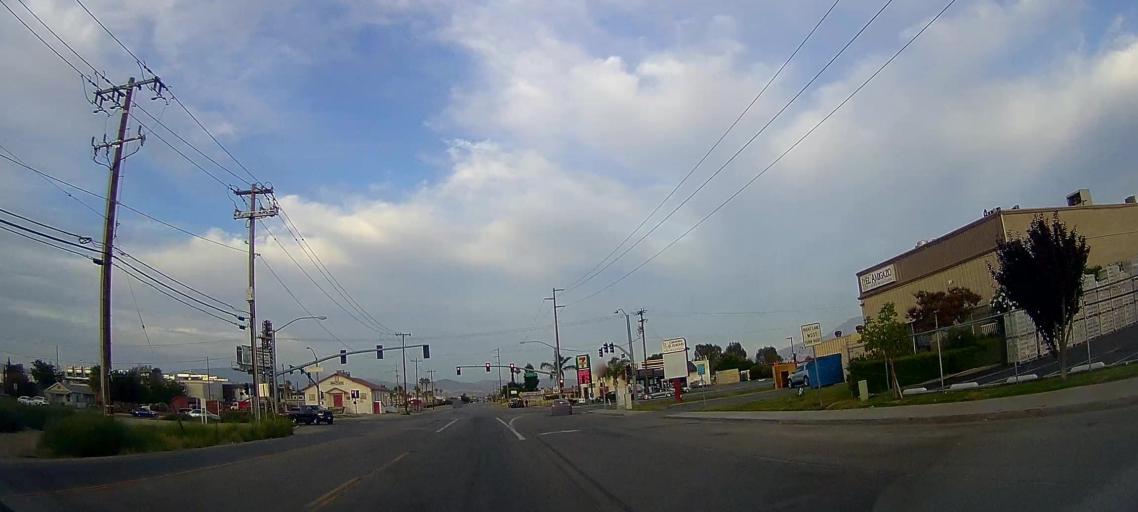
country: US
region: California
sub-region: Kern County
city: Bakersfield
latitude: 35.3543
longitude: -118.9328
